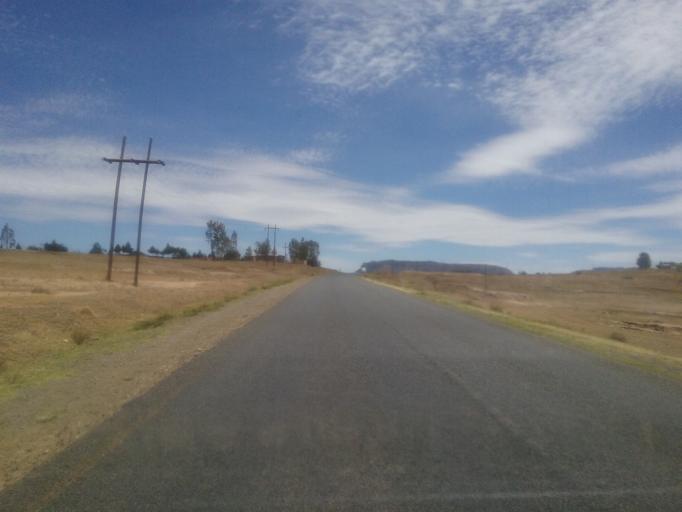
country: LS
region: Mafeteng
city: Mafeteng
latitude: -29.9836
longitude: 27.3249
